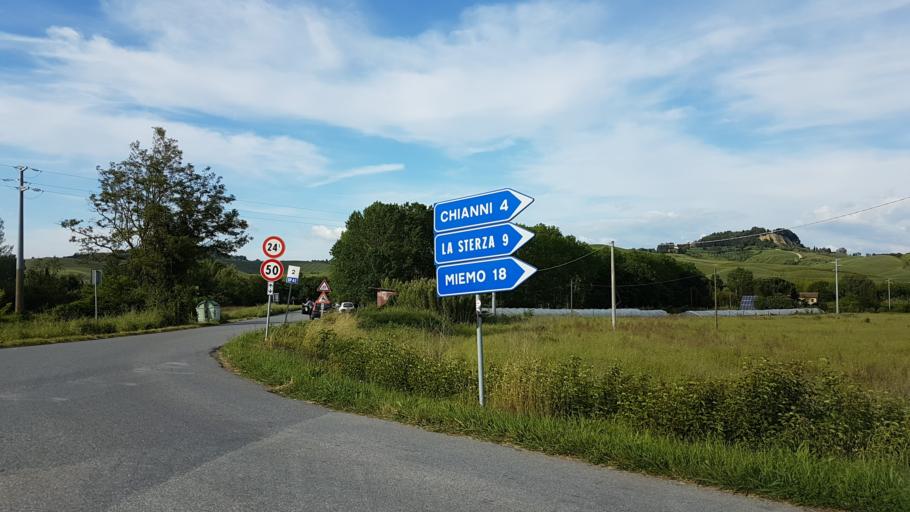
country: IT
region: Tuscany
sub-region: Province of Pisa
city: Terricciola
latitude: 43.5124
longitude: 10.6545
